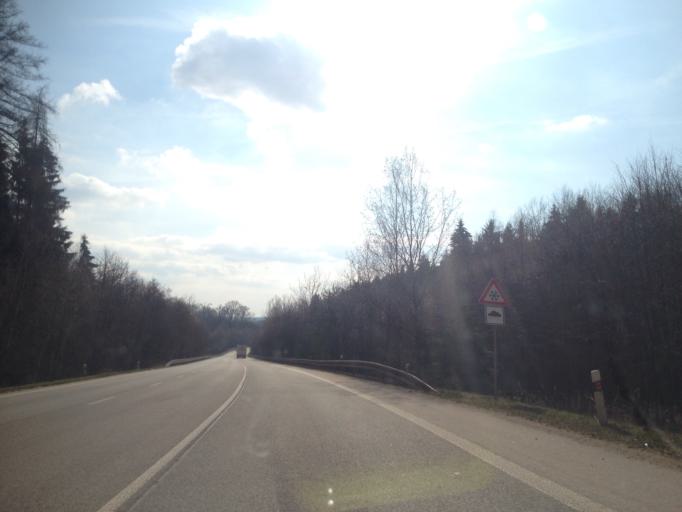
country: CZ
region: Kralovehradecky
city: Nova Paka
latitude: 50.4498
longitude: 15.4708
